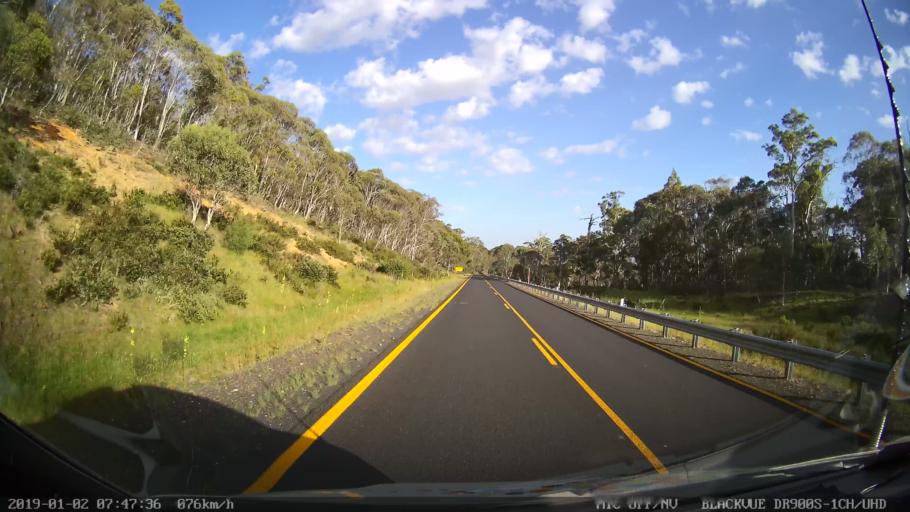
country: AU
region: New South Wales
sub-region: Tumut Shire
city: Tumut
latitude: -35.7631
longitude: 148.5195
